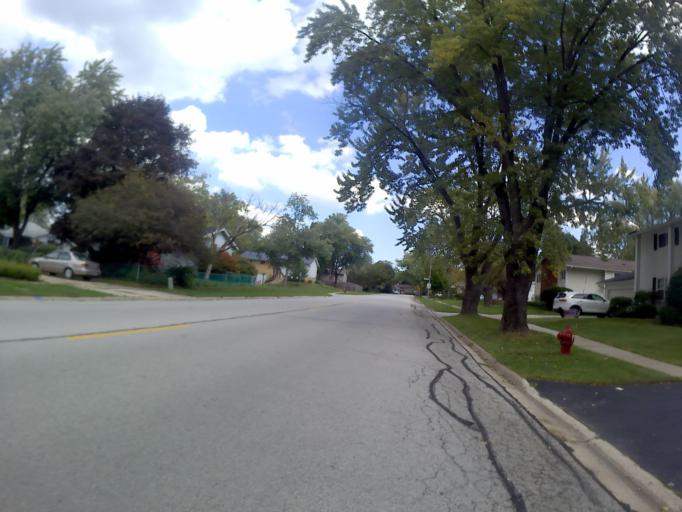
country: US
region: Illinois
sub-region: DuPage County
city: Woodridge
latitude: 41.7690
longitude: -88.0659
